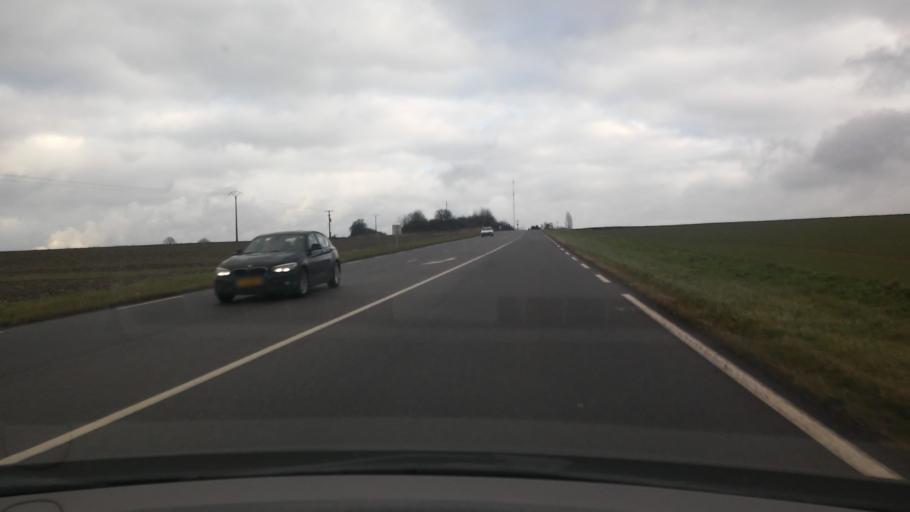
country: FR
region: Lorraine
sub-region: Departement de la Moselle
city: Longeville-les-Saint-Avold
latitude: 49.1203
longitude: 6.6066
